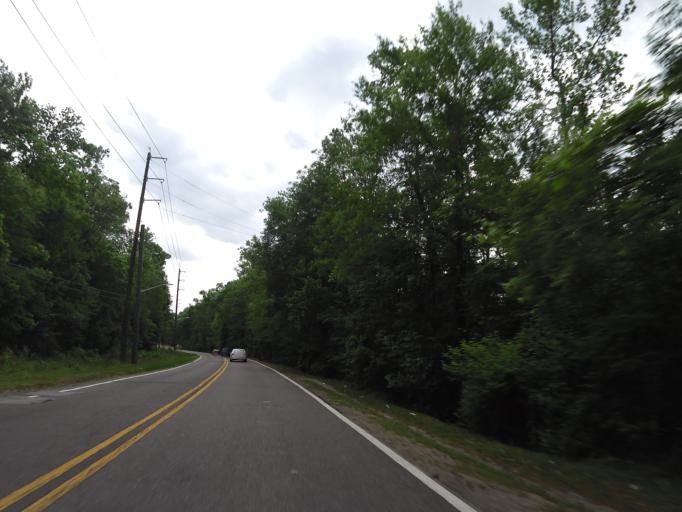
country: US
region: Florida
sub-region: Clay County
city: Bellair-Meadowbrook Terrace
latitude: 30.2026
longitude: -81.7338
